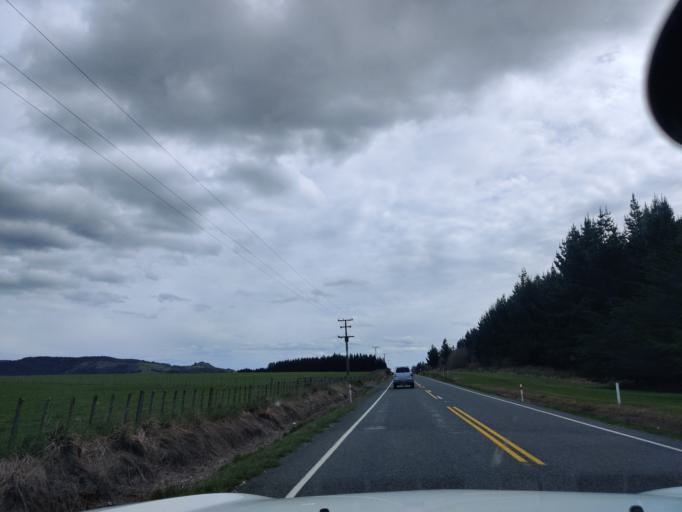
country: NZ
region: Manawatu-Wanganui
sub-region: Ruapehu District
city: Waiouru
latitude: -39.4695
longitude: 175.5632
